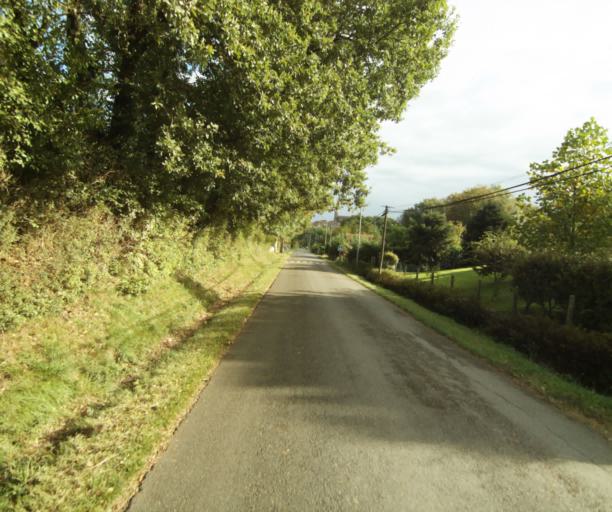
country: FR
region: Midi-Pyrenees
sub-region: Departement du Gers
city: Eauze
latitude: 43.8669
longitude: 0.0968
